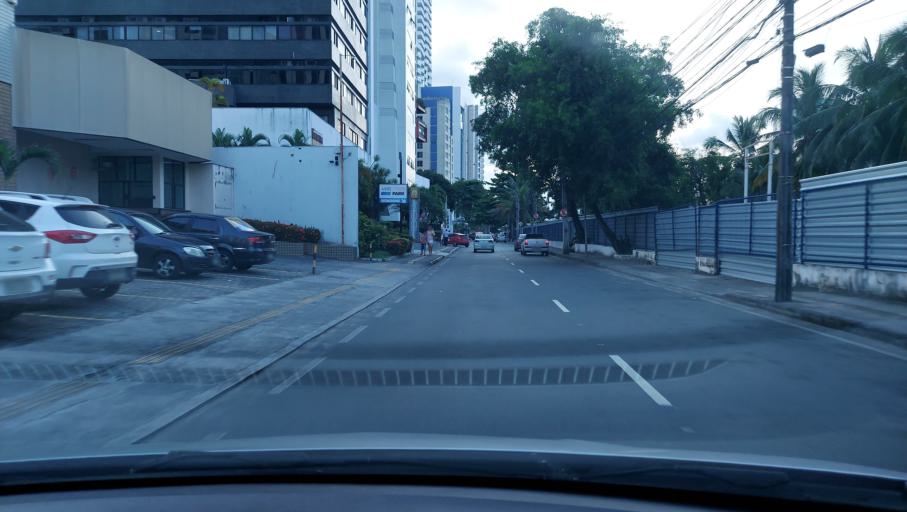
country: BR
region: Bahia
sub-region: Salvador
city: Salvador
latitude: -12.9805
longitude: -38.4543
